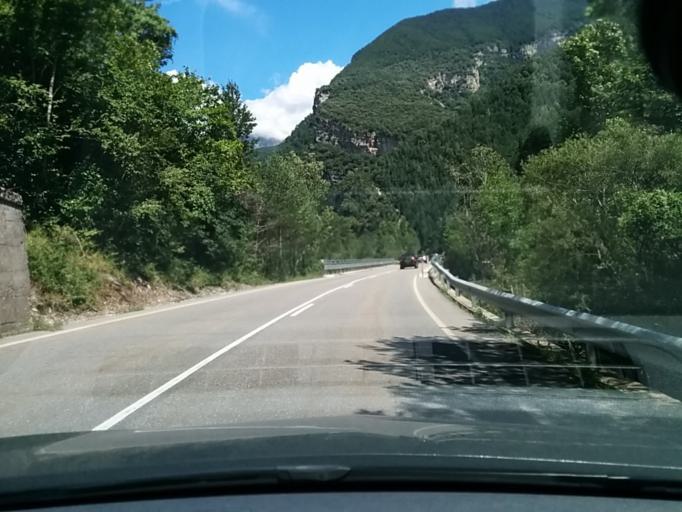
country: ES
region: Aragon
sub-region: Provincia de Huesca
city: Bielsa
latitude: 42.5974
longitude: 0.2378
